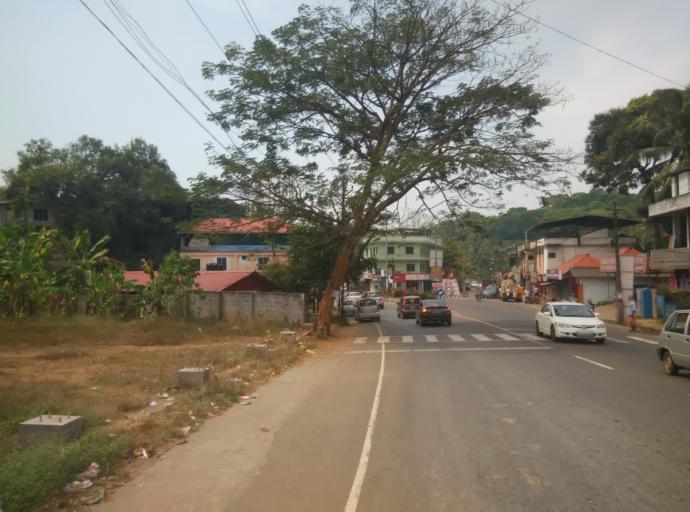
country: IN
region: Kerala
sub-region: Kottayam
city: Lalam
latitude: 9.7012
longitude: 76.6556
